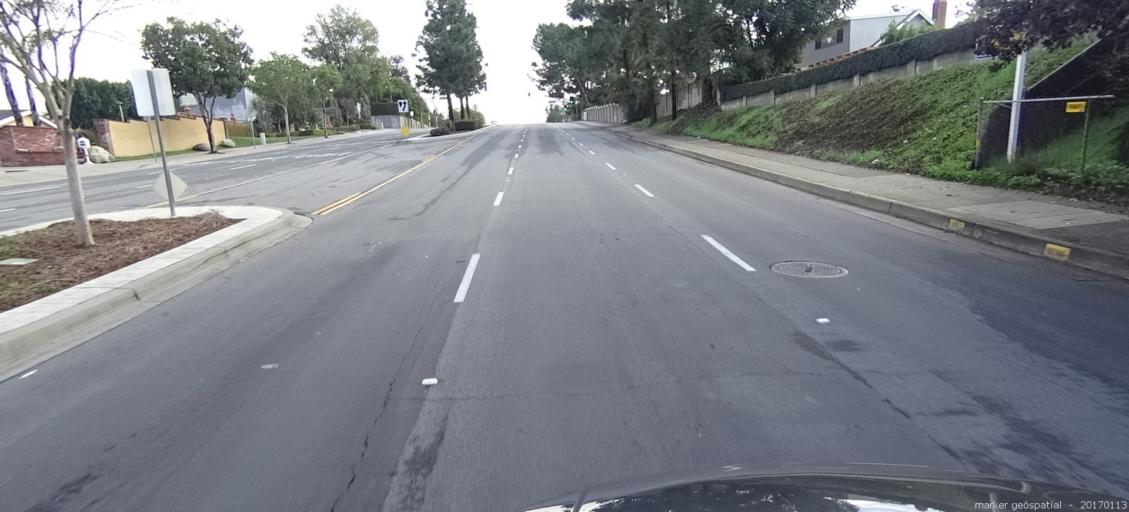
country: US
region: California
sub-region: Orange County
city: Yorba Linda
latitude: 33.8886
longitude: -117.7969
